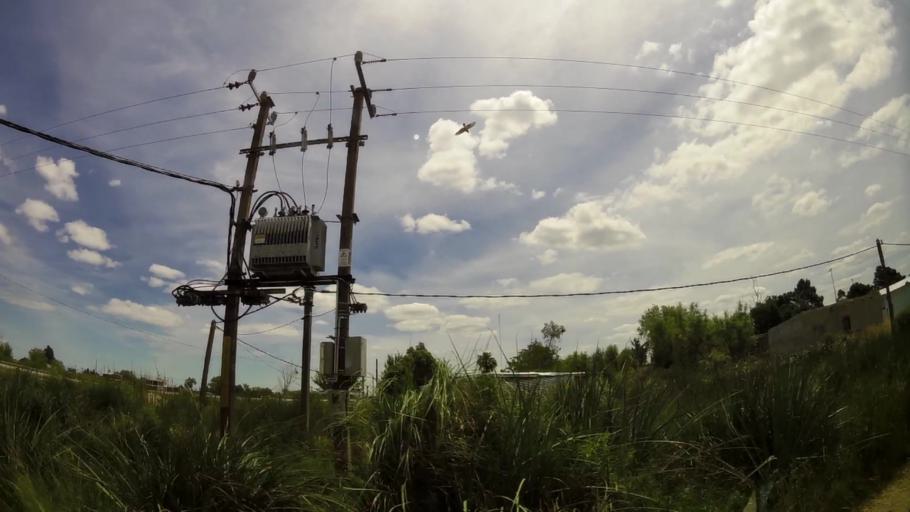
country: UY
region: San Jose
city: Delta del Tigre
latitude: -34.7633
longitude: -56.4076
